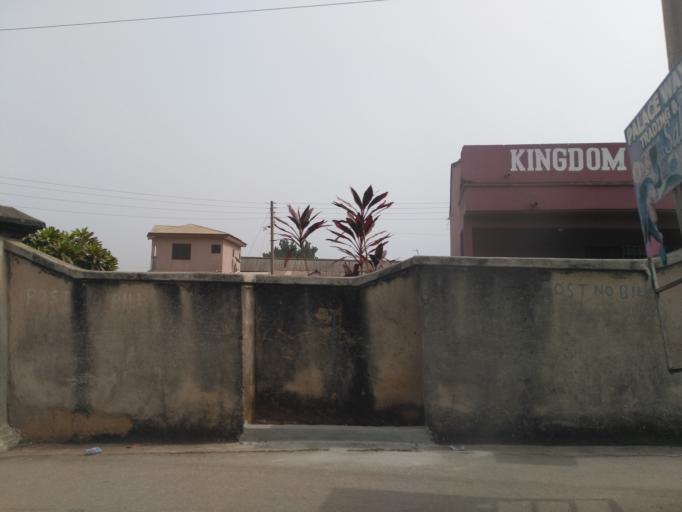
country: GH
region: Ashanti
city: Kumasi
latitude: 6.7045
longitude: -1.6080
